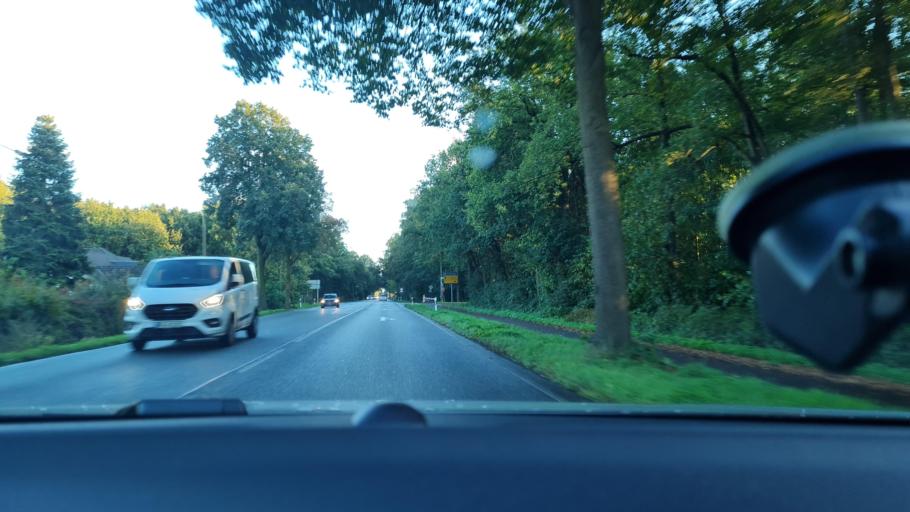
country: DE
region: North Rhine-Westphalia
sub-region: Regierungsbezirk Dusseldorf
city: Voerde
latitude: 51.5975
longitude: 6.7092
